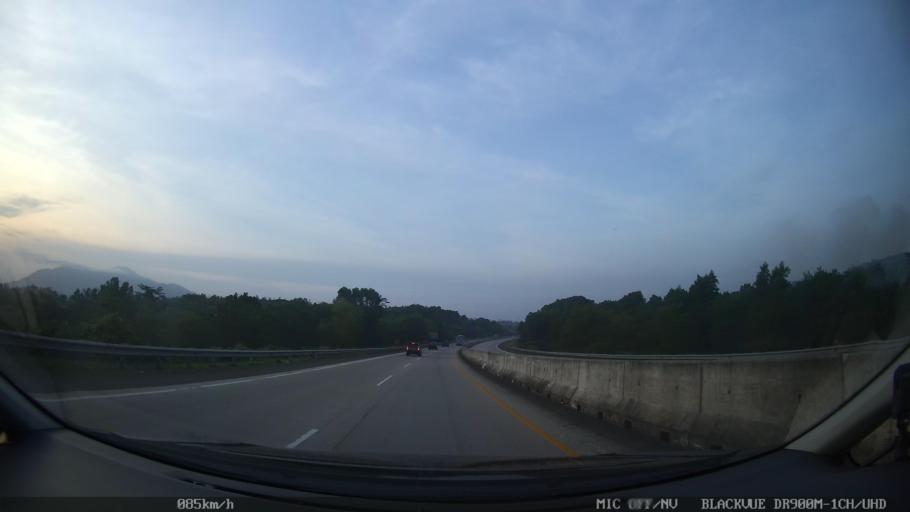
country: ID
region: Lampung
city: Penengahan
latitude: -5.8491
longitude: 105.7273
